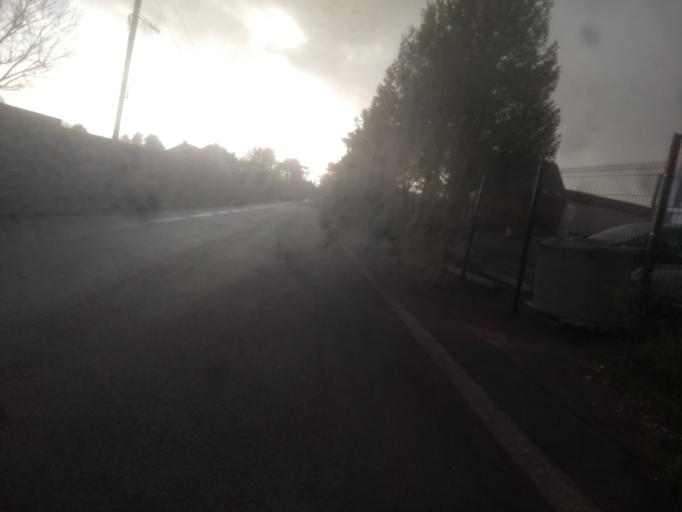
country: FR
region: Nord-Pas-de-Calais
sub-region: Departement du Pas-de-Calais
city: Saint-Laurent-Blangy
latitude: 50.3064
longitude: 2.8074
